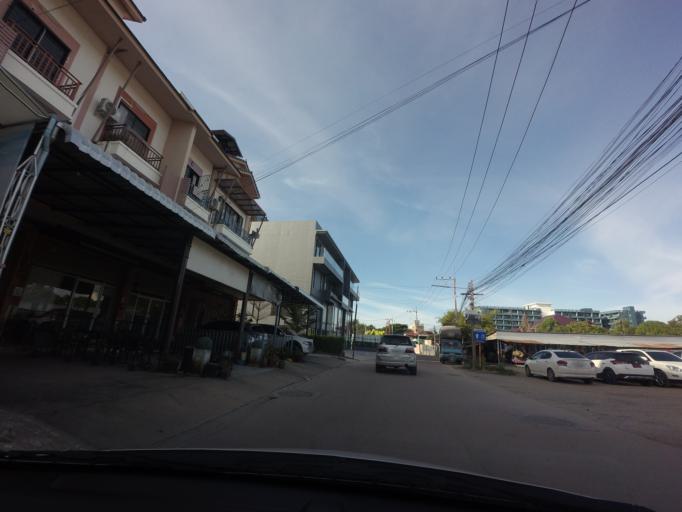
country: TH
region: Chon Buri
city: Sattahip
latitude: 12.7624
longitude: 100.8979
